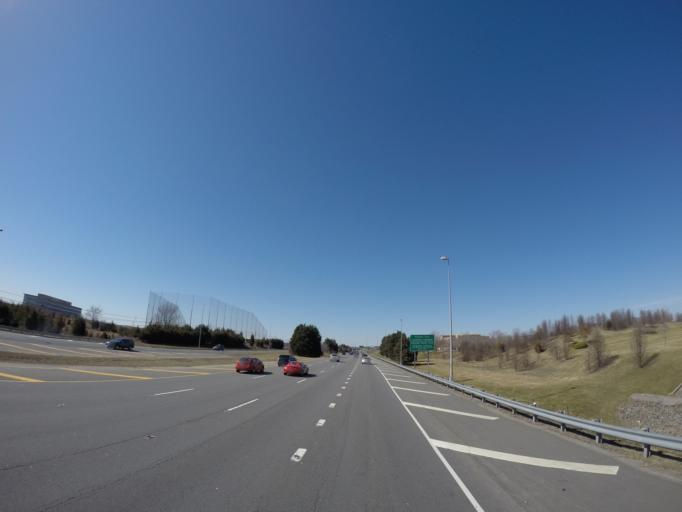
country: US
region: Virginia
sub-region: Loudoun County
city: University Center
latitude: 39.0519
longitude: -77.4411
